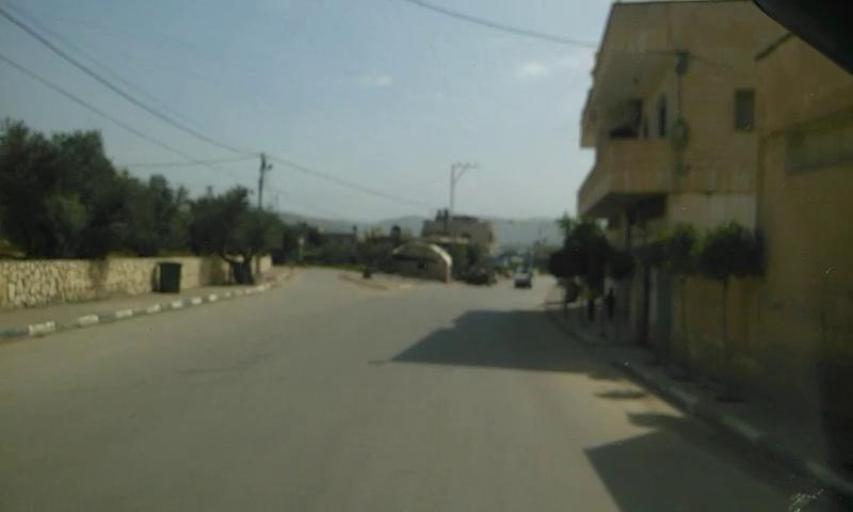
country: PS
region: West Bank
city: Birqin
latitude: 32.4480
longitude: 35.2621
